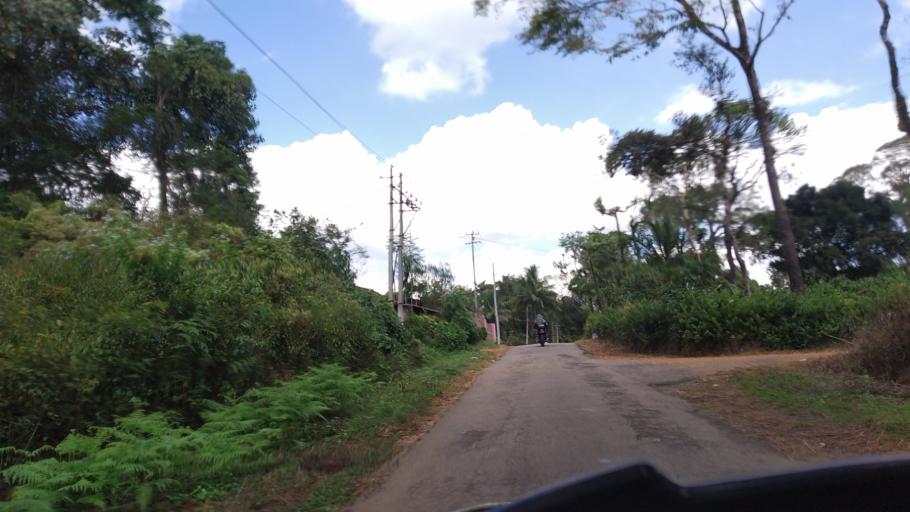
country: IN
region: Karnataka
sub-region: Kodagu
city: Ponnampet
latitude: 12.0254
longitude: 75.8928
